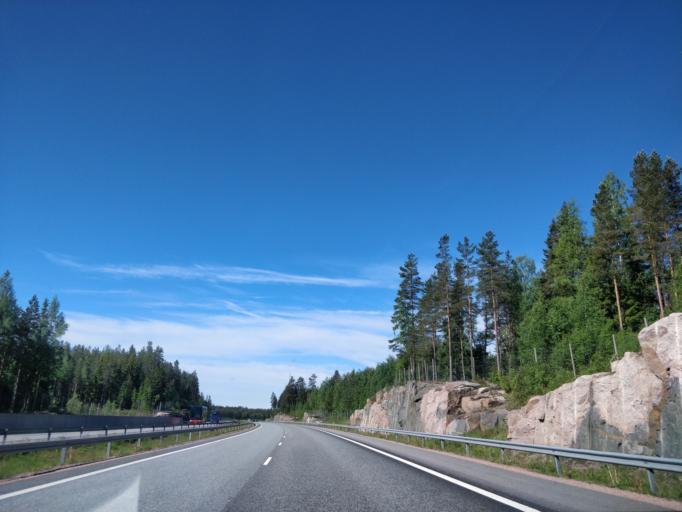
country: FI
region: Varsinais-Suomi
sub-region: Salo
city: Kiikala
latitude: 60.3881
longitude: 23.5077
